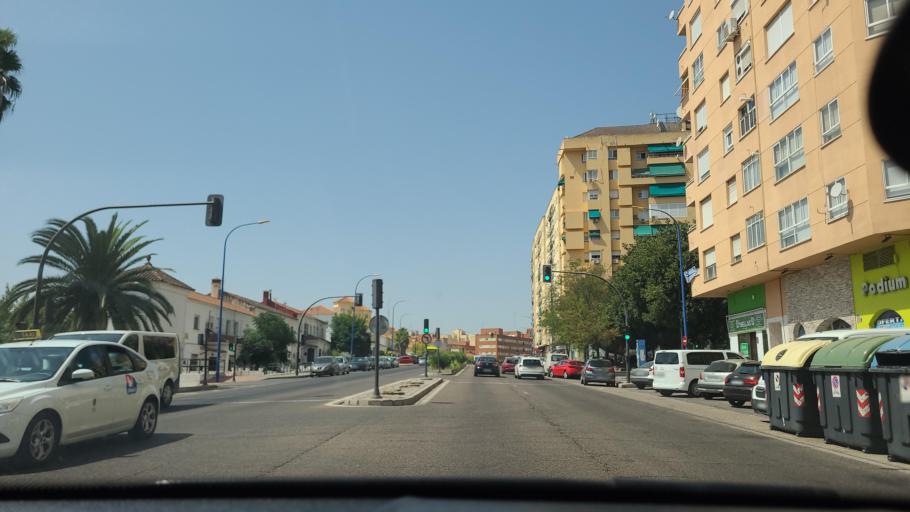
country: ES
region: Extremadura
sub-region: Provincia de Badajoz
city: Badajoz
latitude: 38.8700
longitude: -6.9685
